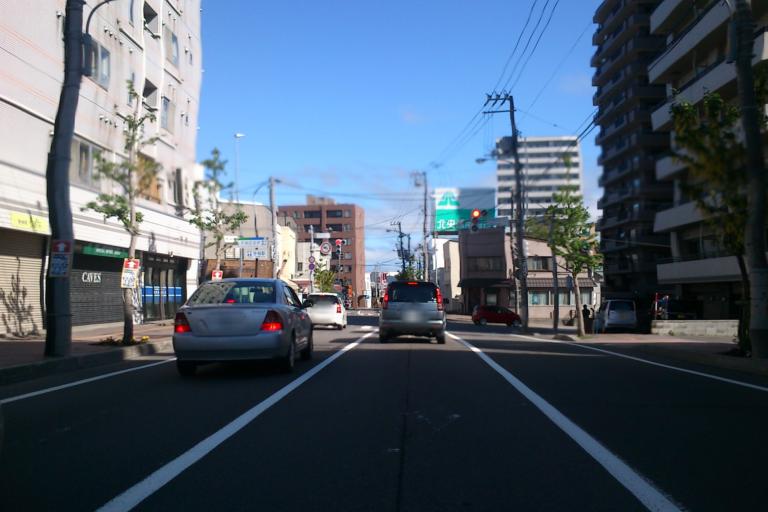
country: JP
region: Hokkaido
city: Sapporo
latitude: 43.1174
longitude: 141.2438
